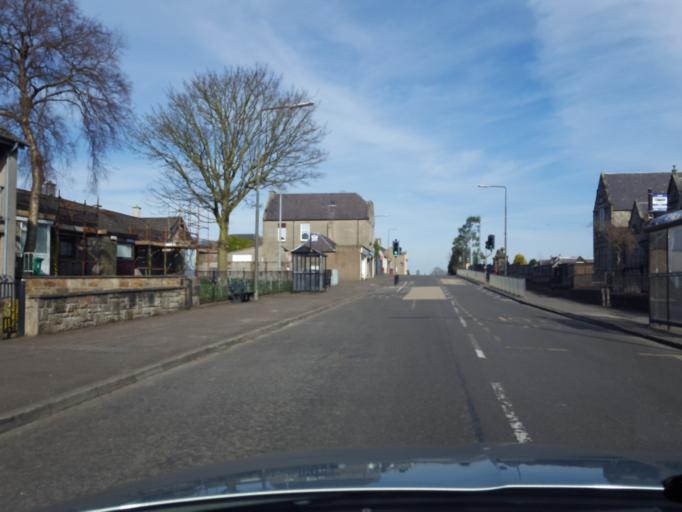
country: GB
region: Scotland
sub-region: Fife
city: Kelty
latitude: 56.1351
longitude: -3.3812
